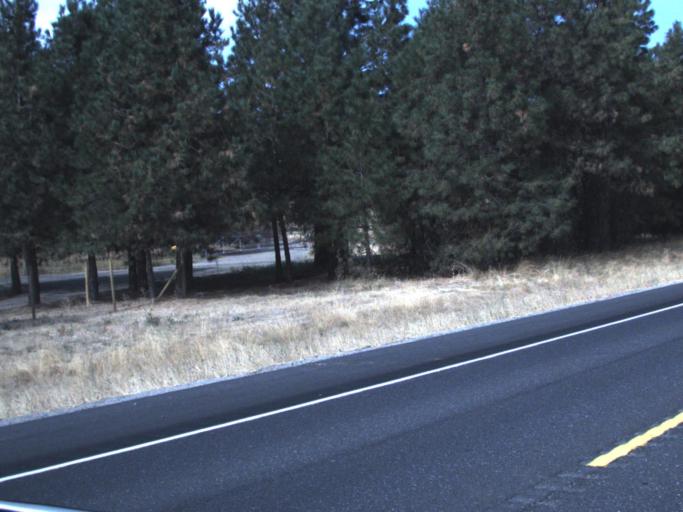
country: US
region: Washington
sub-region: Spokane County
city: Deer Park
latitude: 47.9218
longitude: -117.4572
